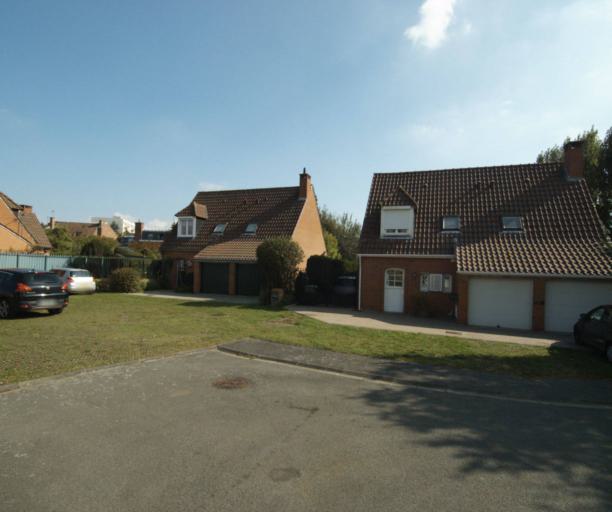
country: FR
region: Nord-Pas-de-Calais
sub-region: Departement du Nord
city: Wattignies
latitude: 50.5840
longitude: 3.0499
